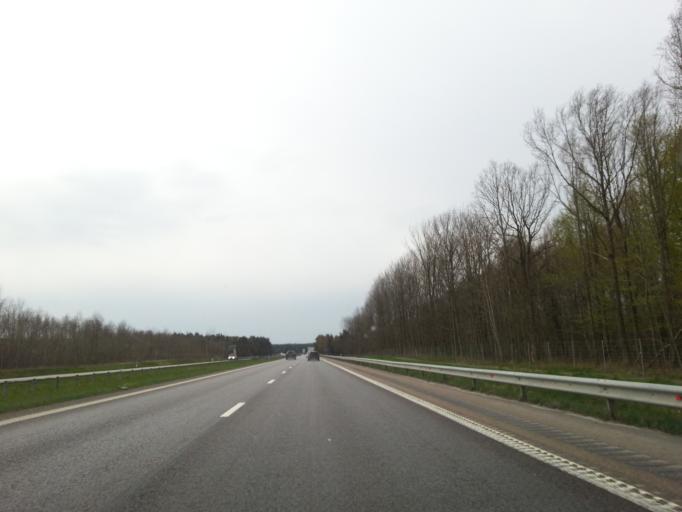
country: SE
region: Halland
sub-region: Laholms Kommun
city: Mellbystrand
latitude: 56.5356
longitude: 12.9692
